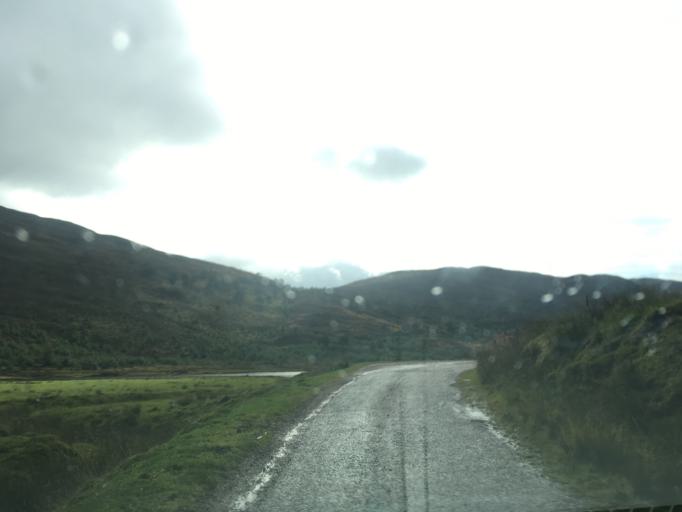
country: GB
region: Scotland
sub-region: Highland
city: Spean Bridge
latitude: 57.3503
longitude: -4.9103
